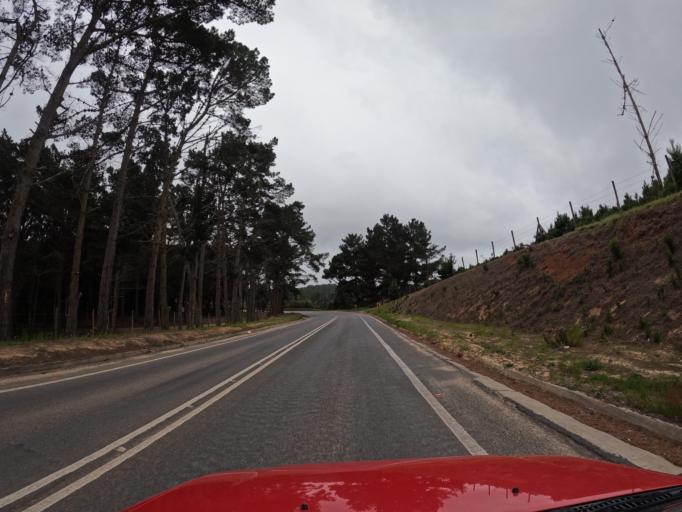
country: CL
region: O'Higgins
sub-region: Provincia de Colchagua
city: Santa Cruz
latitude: -34.5537
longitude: -72.0194
